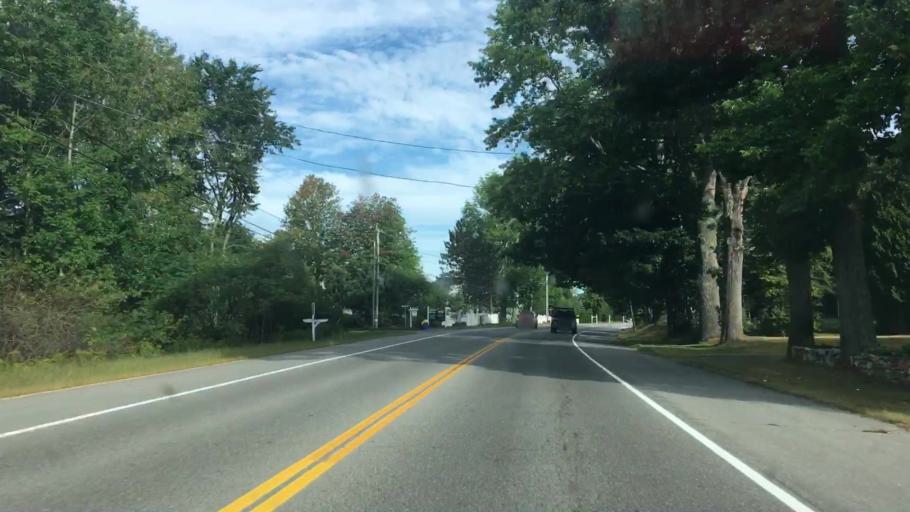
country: US
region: Maine
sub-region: Cumberland County
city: Cumberland Center
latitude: 43.7559
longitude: -70.3005
